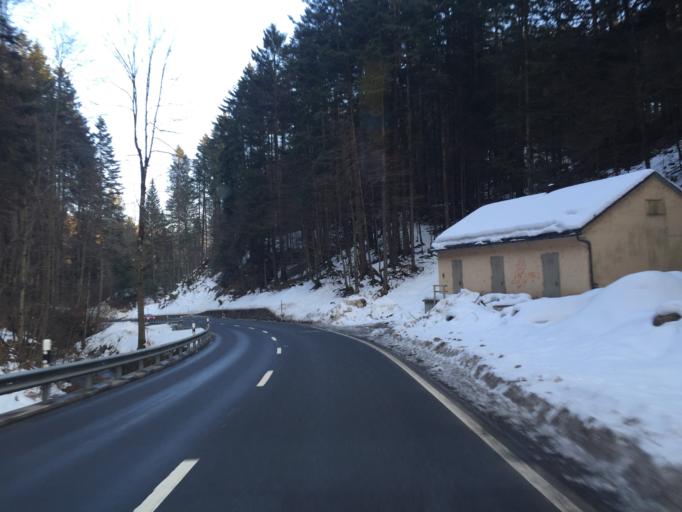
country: CH
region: Saint Gallen
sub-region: Wahlkreis Toggenburg
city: Wildhaus
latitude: 47.1983
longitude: 9.3826
